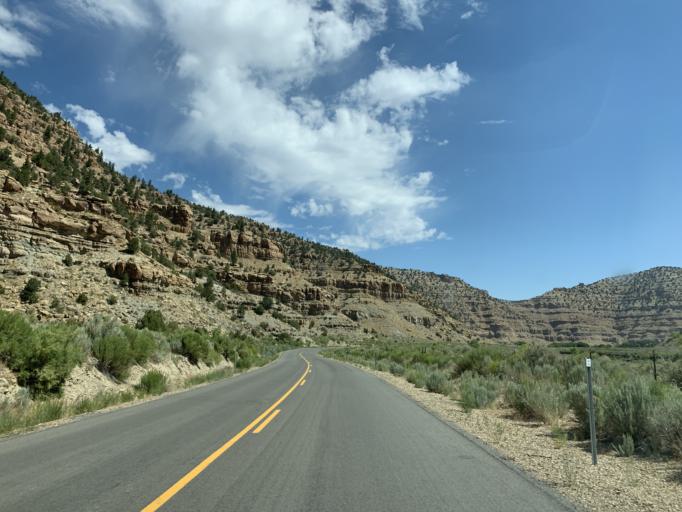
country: US
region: Utah
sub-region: Carbon County
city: East Carbon City
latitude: 39.7930
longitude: -110.3920
